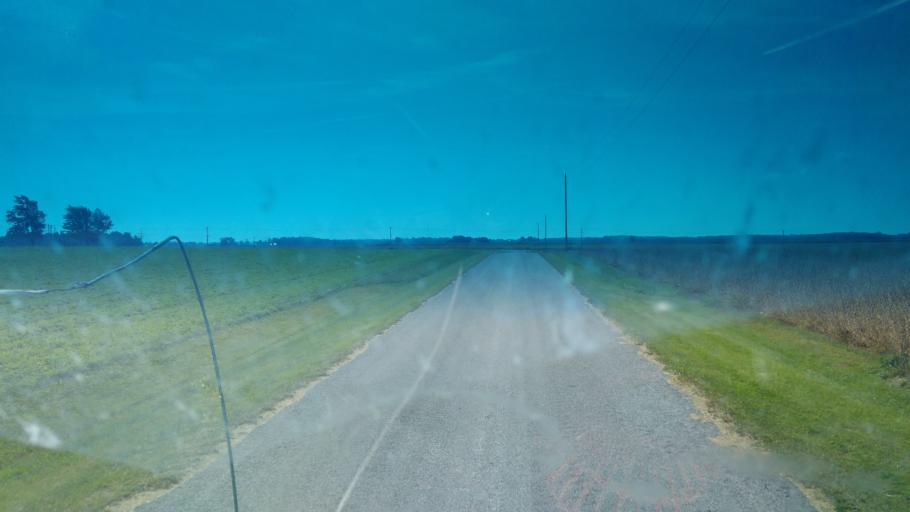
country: US
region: Ohio
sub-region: Marion County
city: Marion
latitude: 40.6610
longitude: -83.2696
